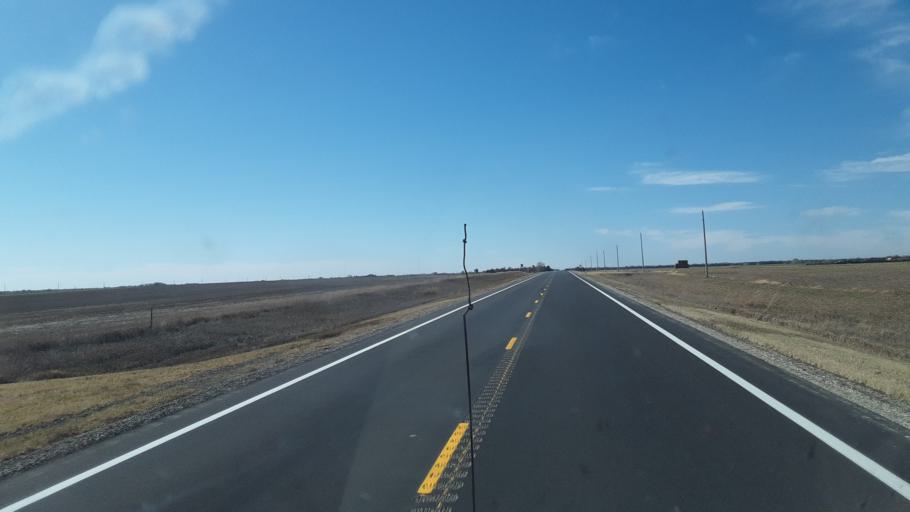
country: US
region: Kansas
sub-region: Rice County
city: Lyons
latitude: 38.3768
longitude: -98.0859
